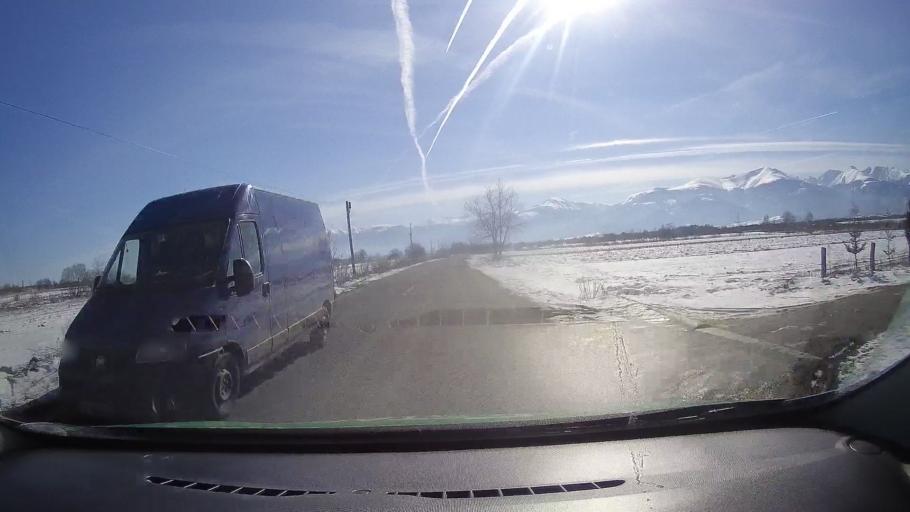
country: RO
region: Brasov
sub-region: Comuna Sambata de Sus
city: Sambata de Sus
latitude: 45.7500
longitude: 24.8374
